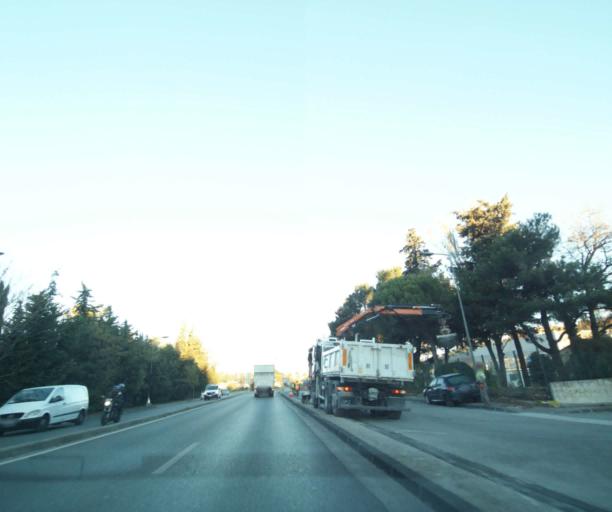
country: FR
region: Provence-Alpes-Cote d'Azur
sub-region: Departement des Bouches-du-Rhone
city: Allauch
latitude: 43.3051
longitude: 5.4712
